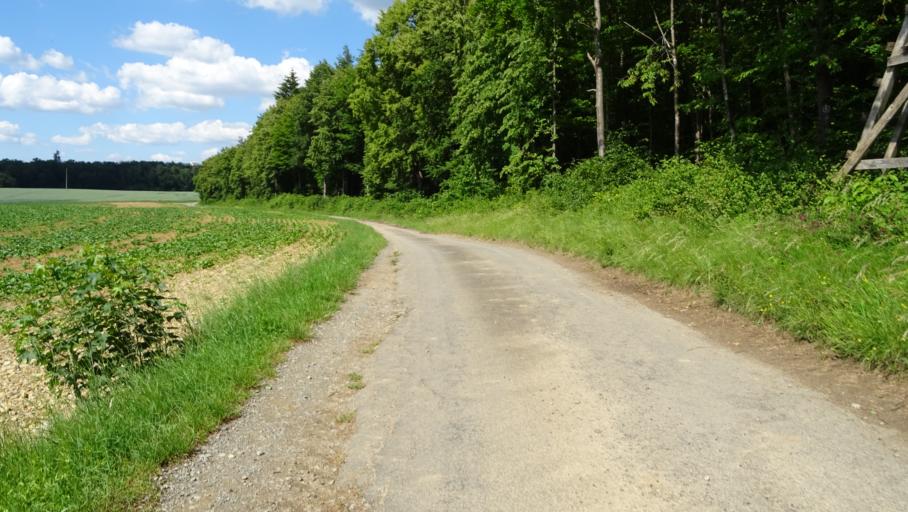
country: DE
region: Baden-Wuerttemberg
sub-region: Karlsruhe Region
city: Adelsheim
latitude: 49.4140
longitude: 9.3668
